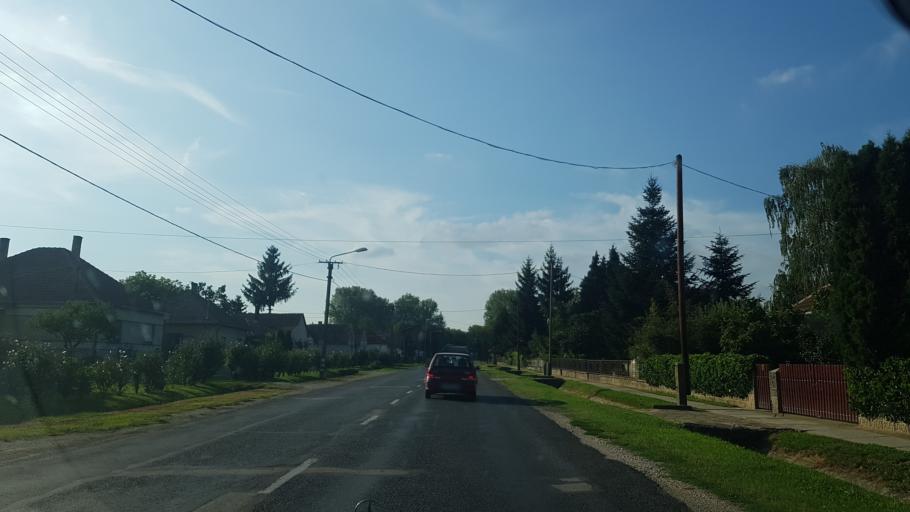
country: HU
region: Somogy
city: Segesd
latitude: 46.2884
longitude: 17.3601
